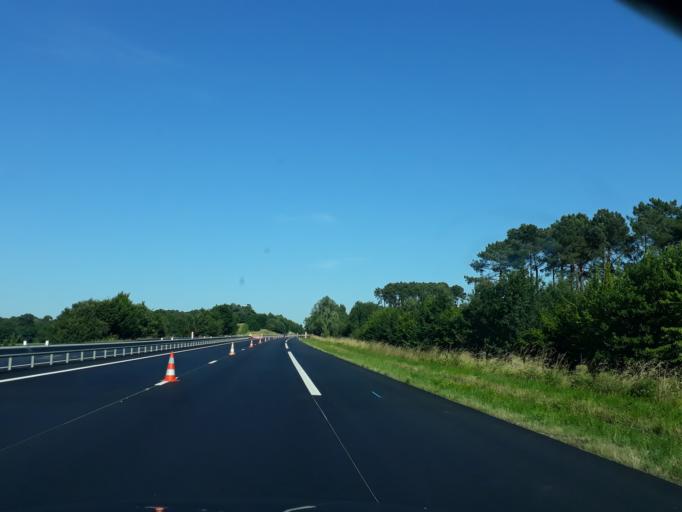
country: FR
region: Aquitaine
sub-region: Departement de la Dordogne
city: Saint-Medard-de-Mussidan
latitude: 45.0087
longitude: 0.3189
